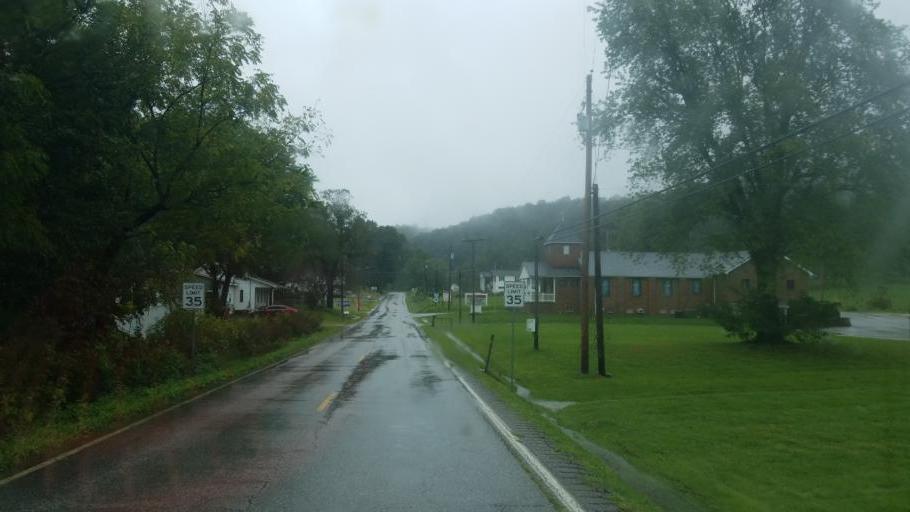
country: US
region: Kentucky
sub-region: Greenup County
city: South Shore
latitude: 38.7068
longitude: -82.9483
